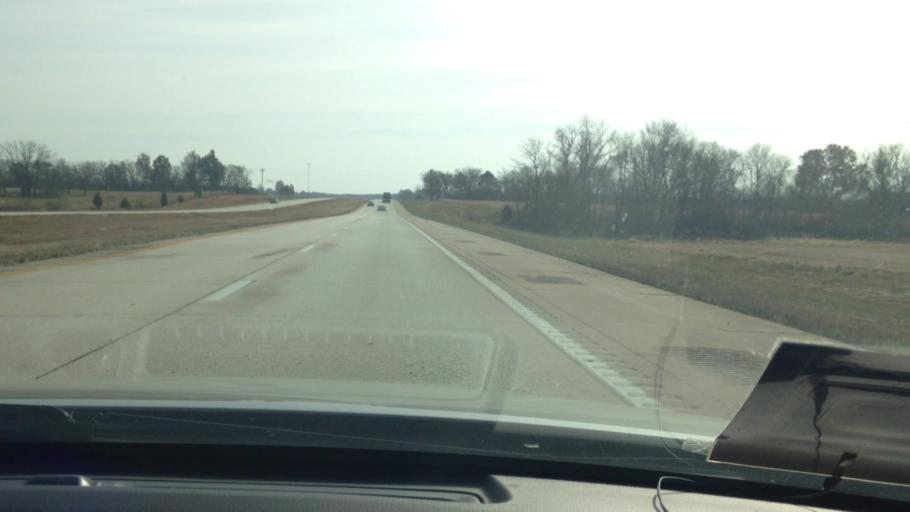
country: US
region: Missouri
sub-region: Henry County
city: Clinton
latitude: 38.4612
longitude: -93.9689
